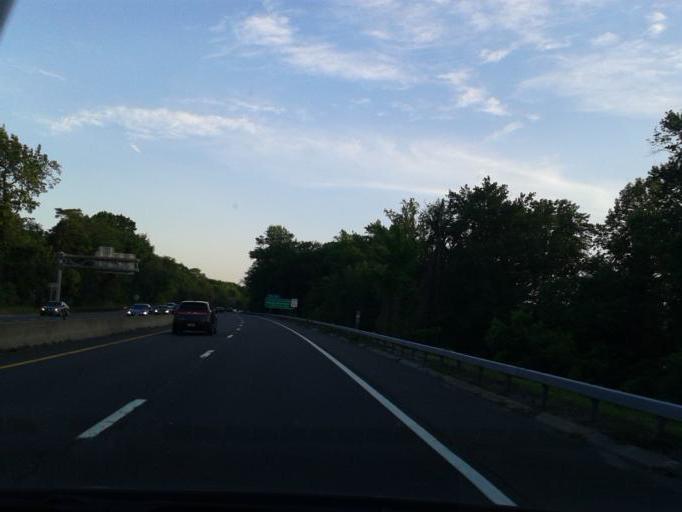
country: US
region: New York
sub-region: Westchester County
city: Tuckahoe
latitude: 40.9489
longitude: -73.7984
